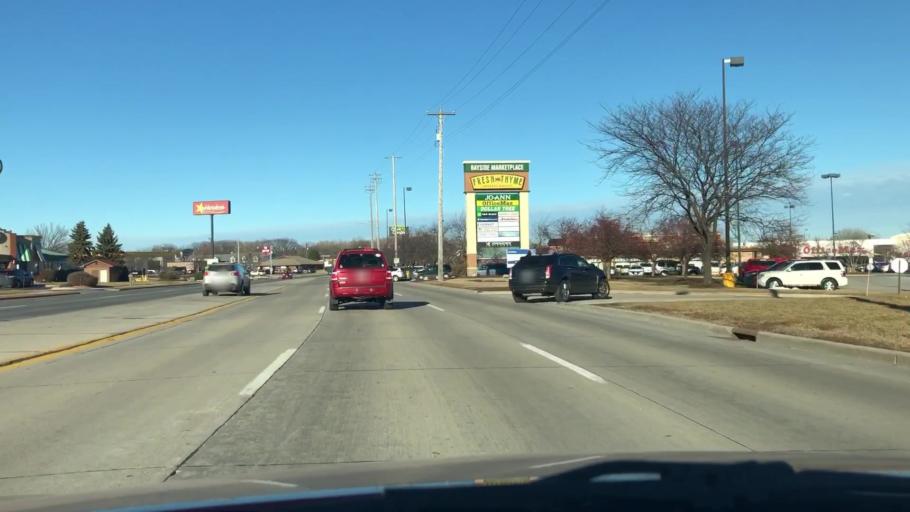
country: US
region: Wisconsin
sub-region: Brown County
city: Ashwaubenon
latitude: 44.4729
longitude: -88.0749
